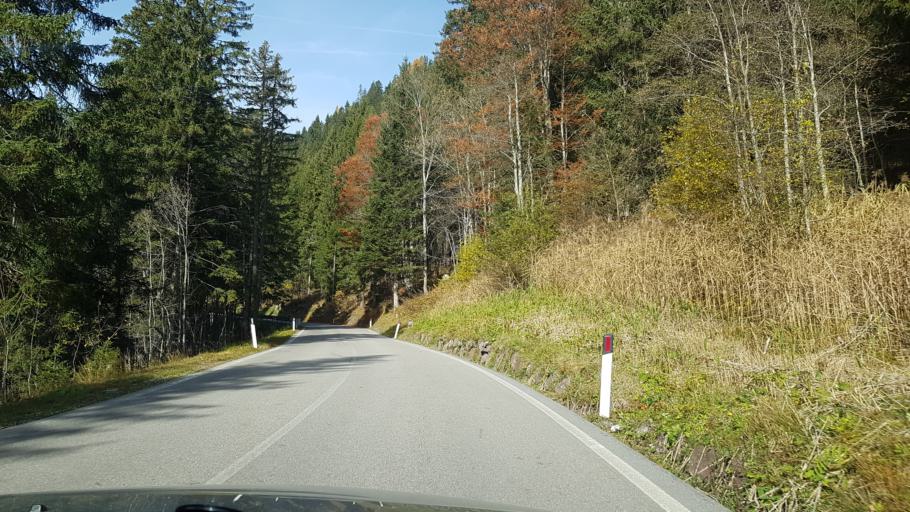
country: IT
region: Veneto
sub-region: Provincia di Belluno
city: Candide
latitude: 46.6517
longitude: 12.4475
